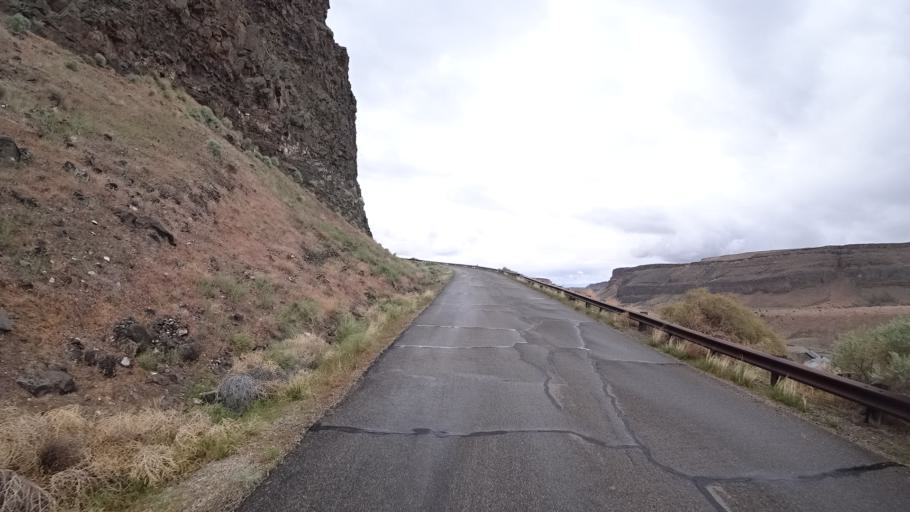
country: US
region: Idaho
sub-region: Owyhee County
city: Murphy
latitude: 43.2469
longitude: -116.3743
